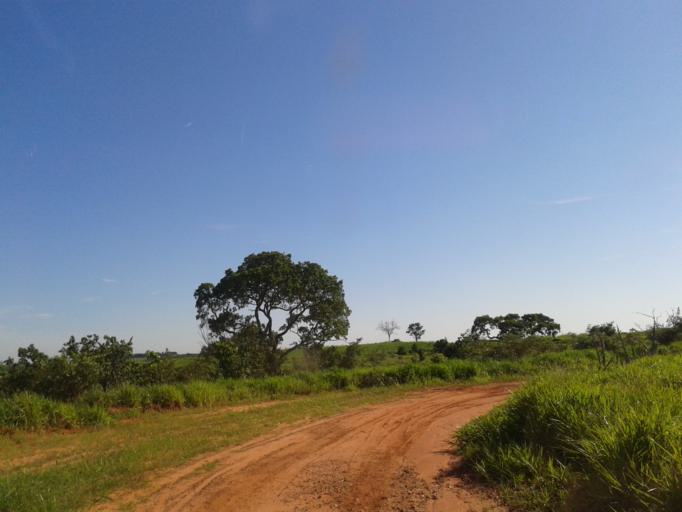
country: BR
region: Minas Gerais
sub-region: Santa Vitoria
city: Santa Vitoria
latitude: -19.1125
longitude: -49.9909
